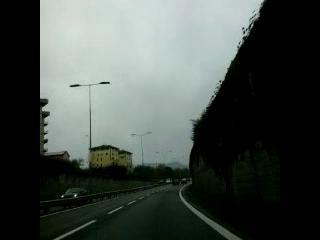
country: IT
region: Lombardy
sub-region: Provincia di Brescia
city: Fantasina
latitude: 45.5471
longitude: 10.1866
